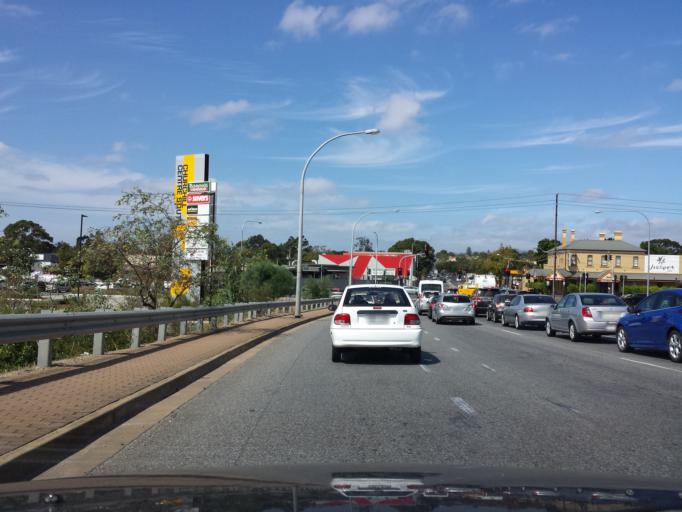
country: AU
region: South Australia
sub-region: Prospect
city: Prospect
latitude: -34.8744
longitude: 138.5831
